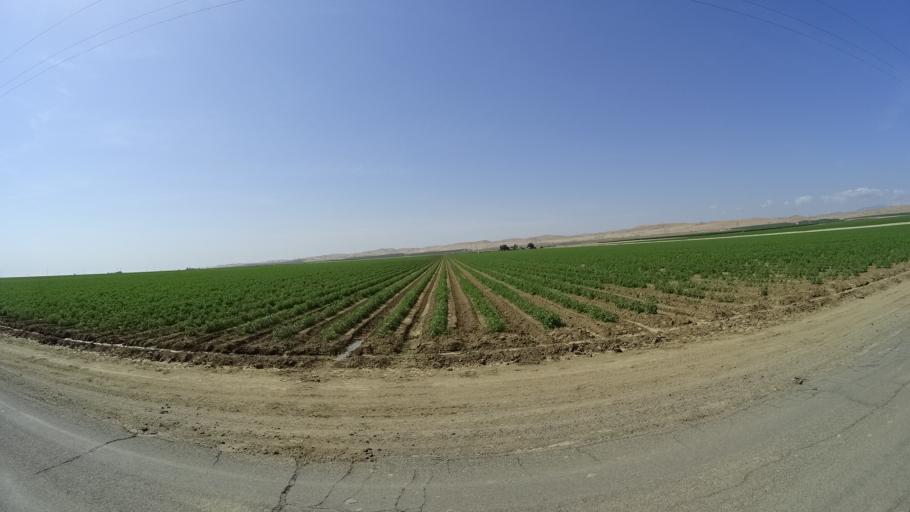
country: US
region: California
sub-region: Kings County
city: Kettleman City
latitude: 36.0725
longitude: -120.0377
